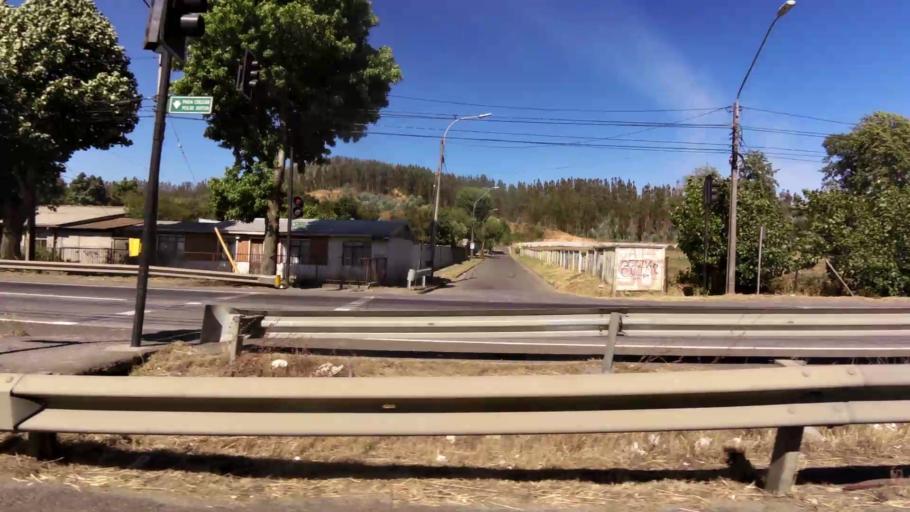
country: CL
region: Biobio
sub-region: Provincia de Concepcion
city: Concepcion
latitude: -36.7943
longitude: -73.0256
